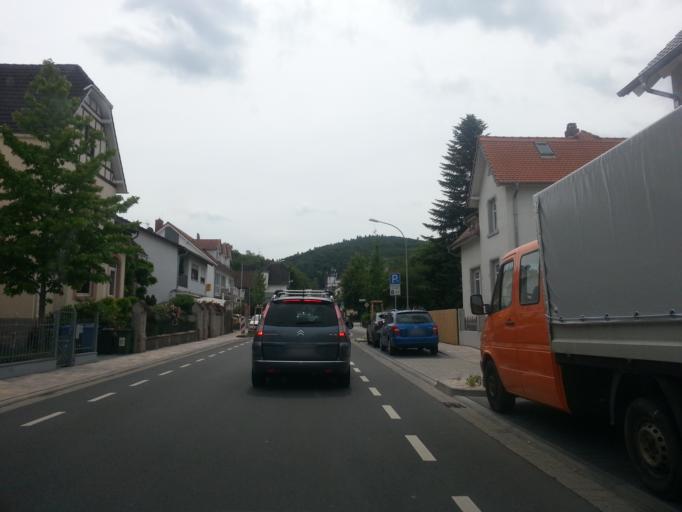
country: DE
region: Hesse
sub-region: Regierungsbezirk Darmstadt
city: Bickenbach
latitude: 49.7562
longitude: 8.6354
